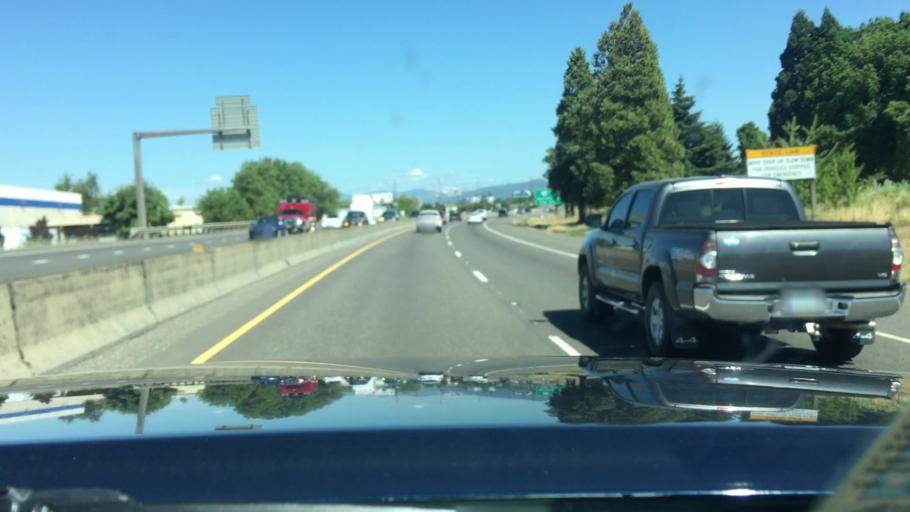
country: US
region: Oregon
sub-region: Lane County
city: Springfield
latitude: 44.0631
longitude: -123.0354
